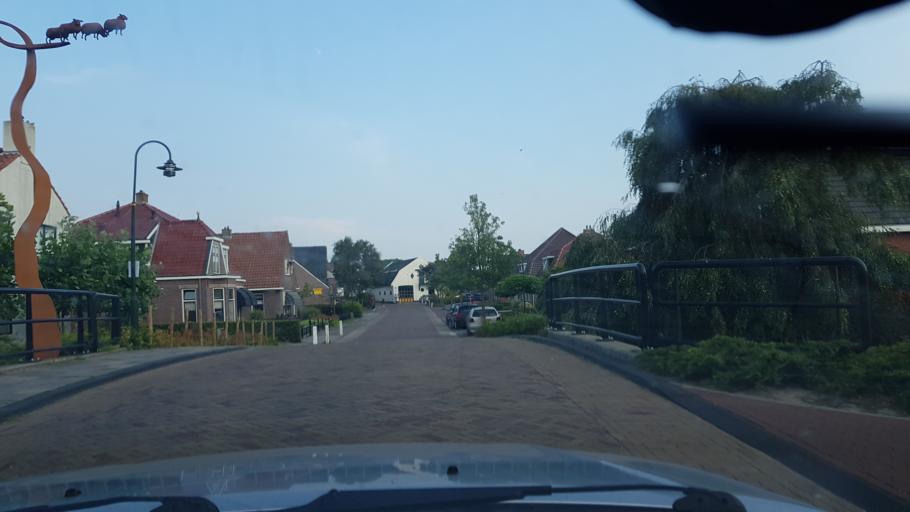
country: NL
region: Friesland
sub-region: Gemeente Ferwerderadiel
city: Burdaard
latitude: 53.2964
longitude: 5.8783
